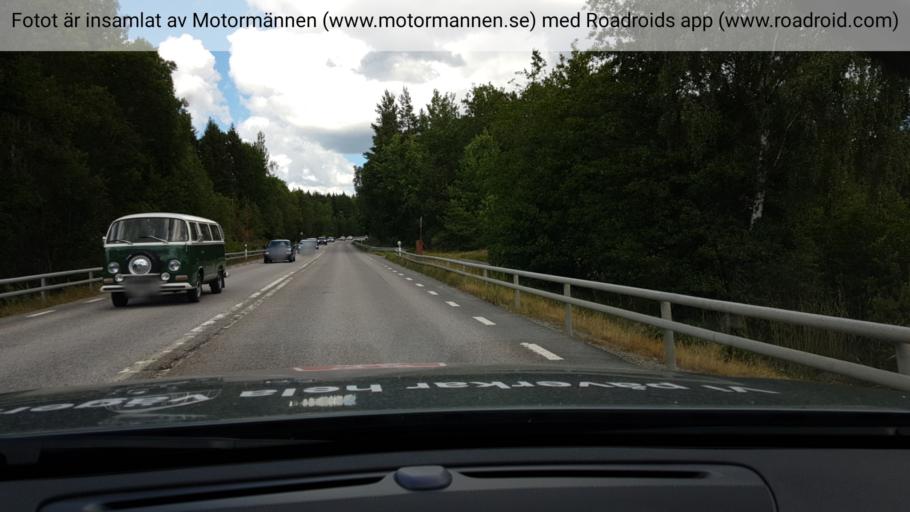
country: SE
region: Stockholm
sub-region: Lidingo
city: Brevik
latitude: 59.4319
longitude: 18.2196
